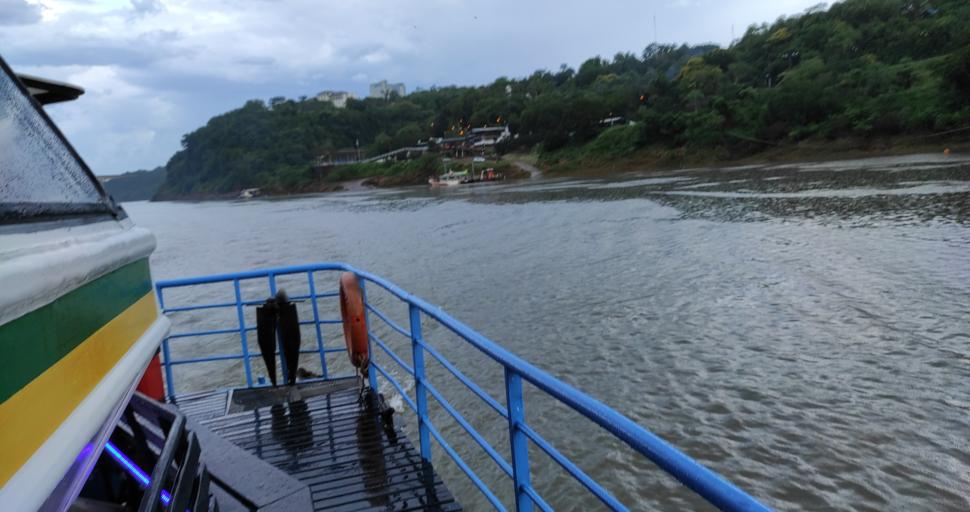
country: AR
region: Misiones
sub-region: Departamento de Iguazu
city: Puerto Iguazu
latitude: -25.5928
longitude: -54.5824
